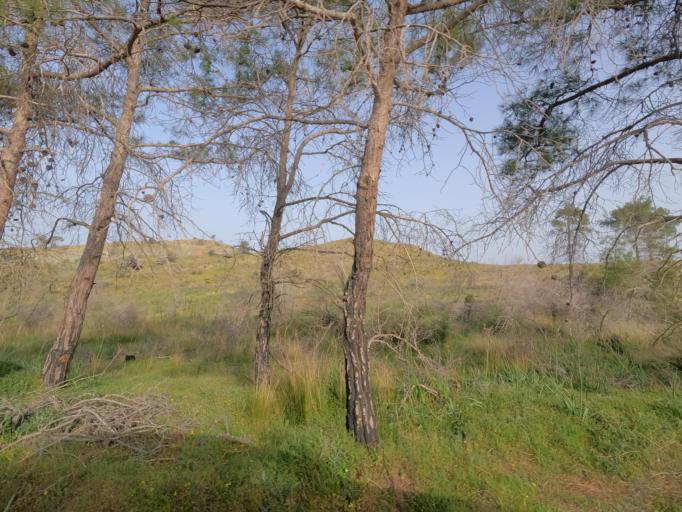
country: CY
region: Pafos
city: Polis
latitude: 34.9940
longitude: 32.3327
